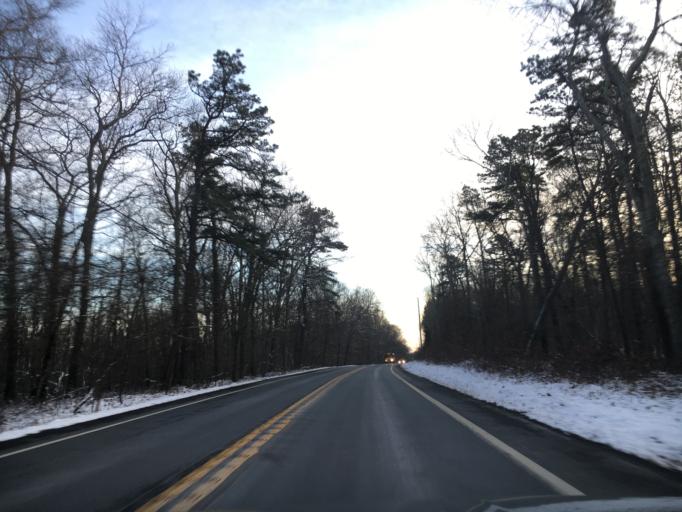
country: US
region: Pennsylvania
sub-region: Pike County
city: Saw Creek
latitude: 41.1964
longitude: -75.0817
